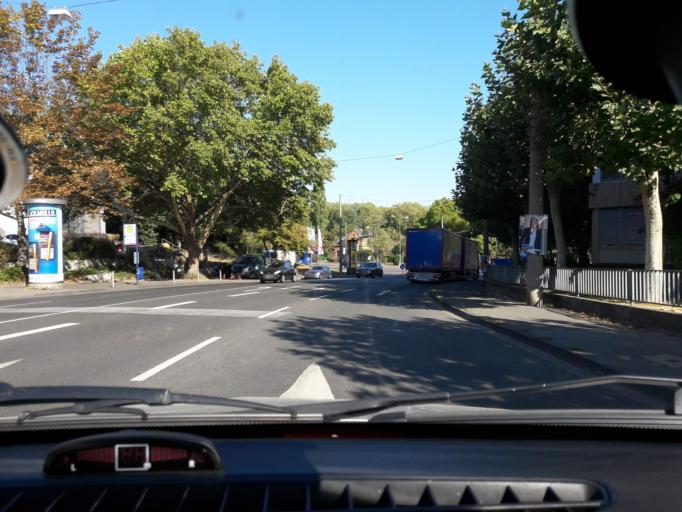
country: DE
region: Hesse
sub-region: Regierungsbezirk Darmstadt
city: Wiesbaden
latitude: 50.0805
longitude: 8.2188
